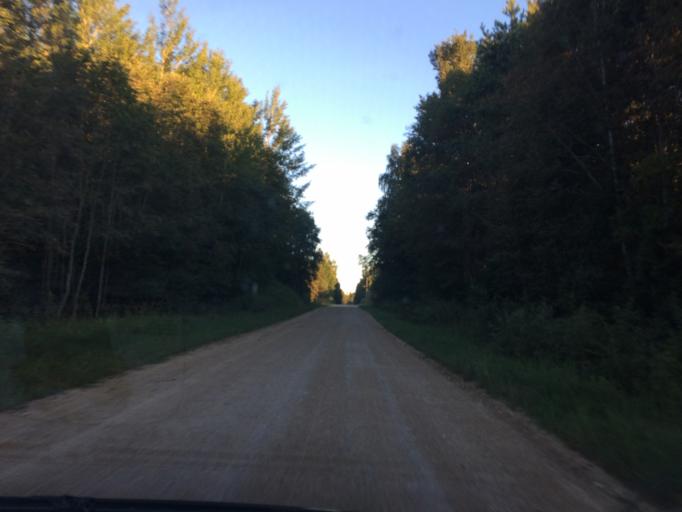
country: LV
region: Preilu Rajons
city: Jaunaglona
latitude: 56.2271
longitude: 27.2205
